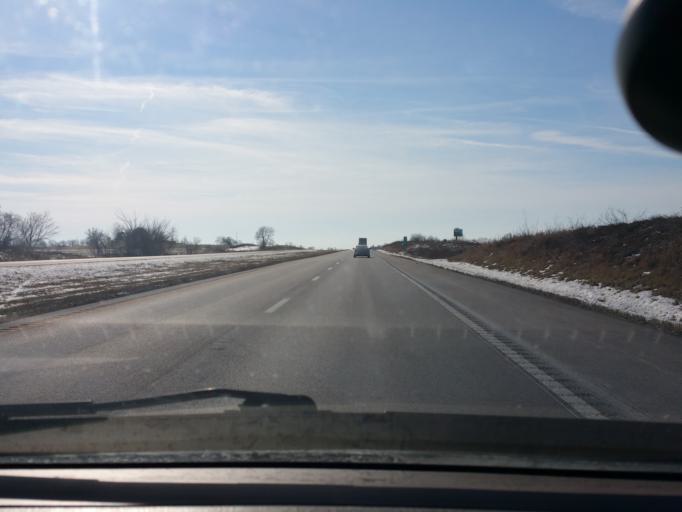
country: US
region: Missouri
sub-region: Clinton County
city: Cameron
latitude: 39.8012
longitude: -94.2000
